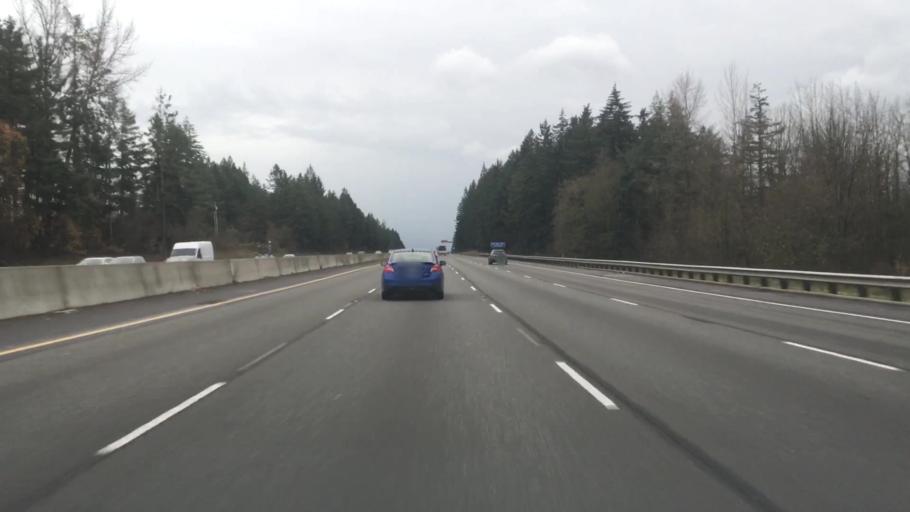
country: US
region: Washington
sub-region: Thurston County
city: Grand Mound
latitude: 46.8867
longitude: -122.9642
